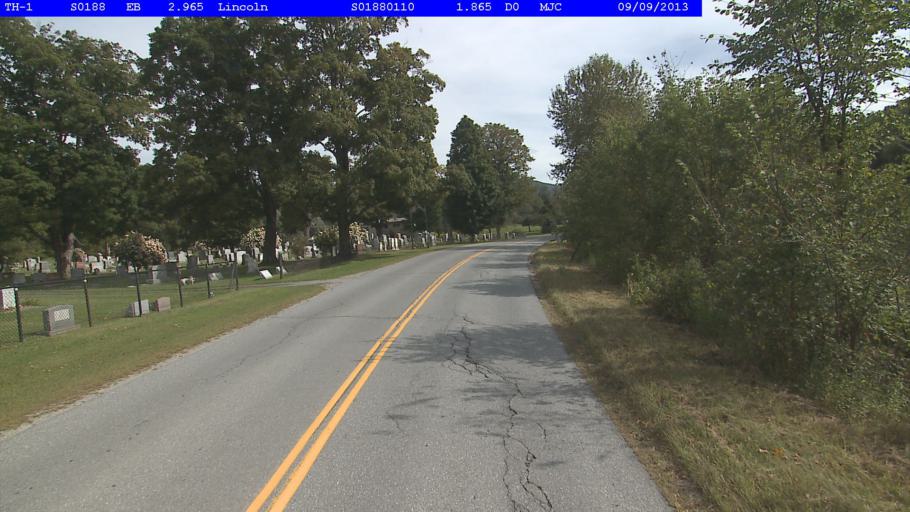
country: US
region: Vermont
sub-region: Addison County
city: Bristol
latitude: 44.1101
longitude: -73.0014
